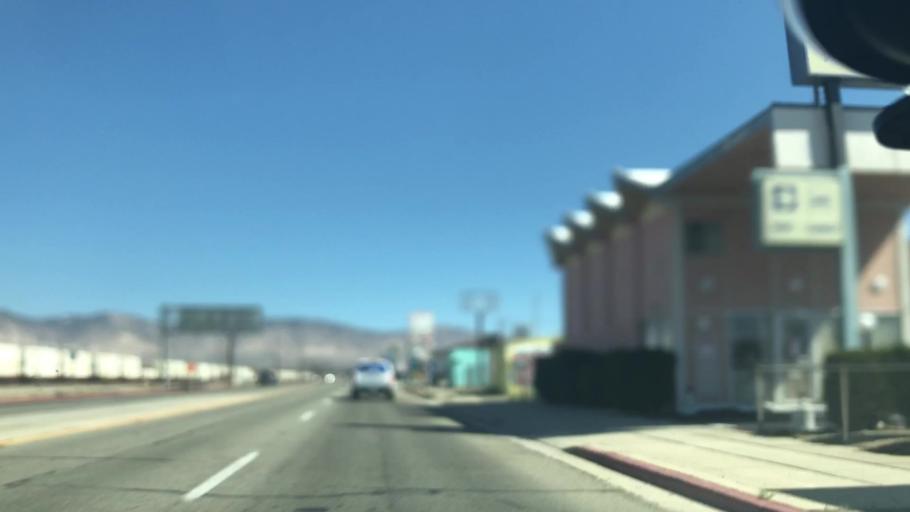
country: US
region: California
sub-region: Kern County
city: Mojave
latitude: 35.0487
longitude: -118.1724
